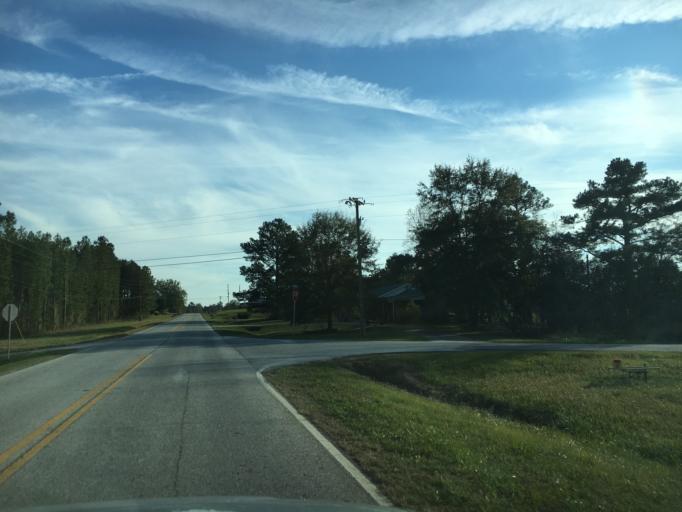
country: US
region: Georgia
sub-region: Elbert County
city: Elberton
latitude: 34.0292
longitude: -82.7934
